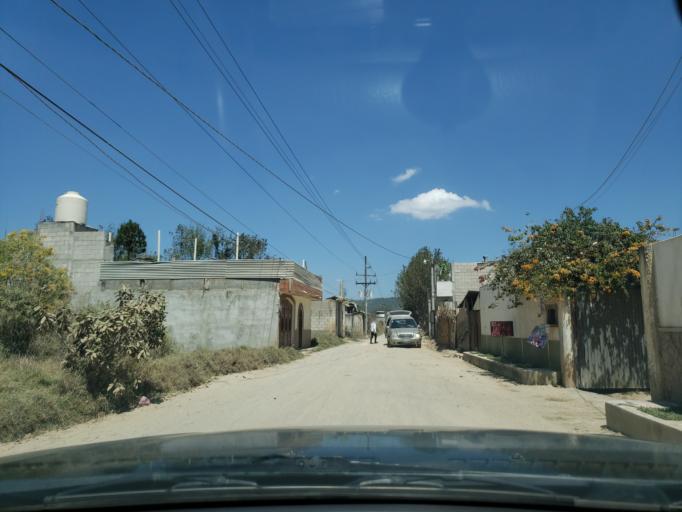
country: GT
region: Chimaltenango
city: El Tejar
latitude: 14.6476
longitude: -90.8038
